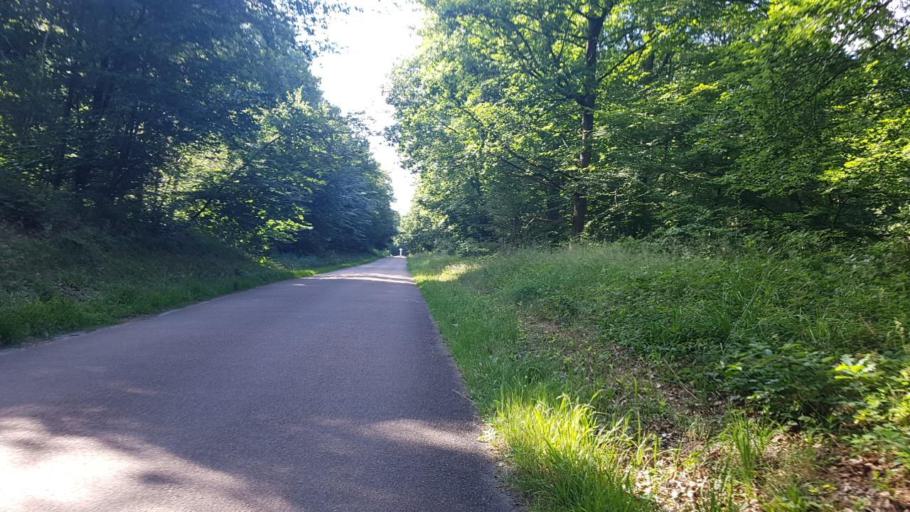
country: FR
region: Picardie
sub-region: Departement de l'Oise
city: Ver-sur-Launette
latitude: 49.1496
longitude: 2.6424
